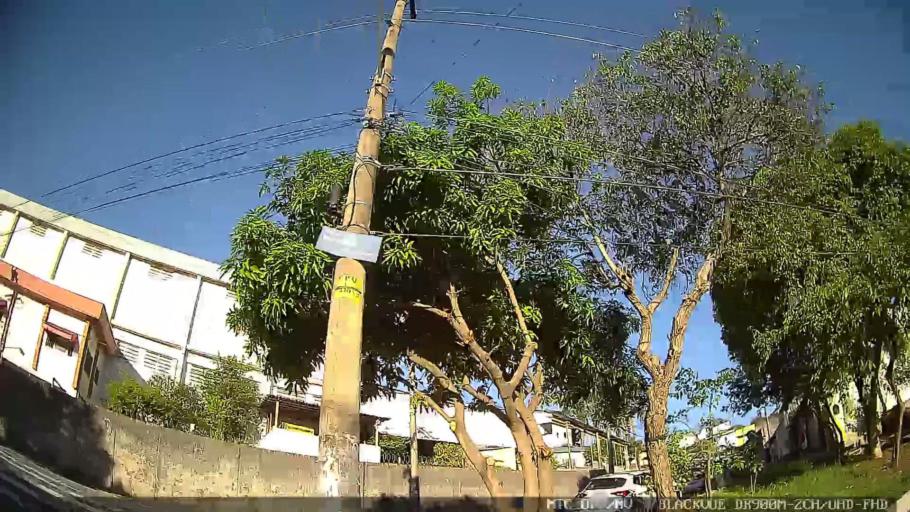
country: BR
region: Sao Paulo
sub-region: Guarulhos
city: Guarulhos
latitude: -23.5330
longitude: -46.5196
